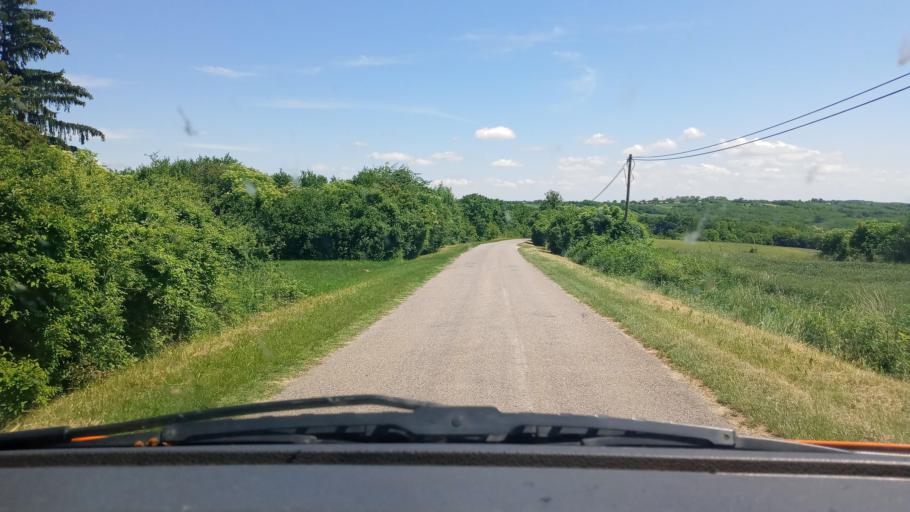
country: HU
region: Baranya
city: Szigetvar
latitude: 46.1738
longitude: 17.7481
